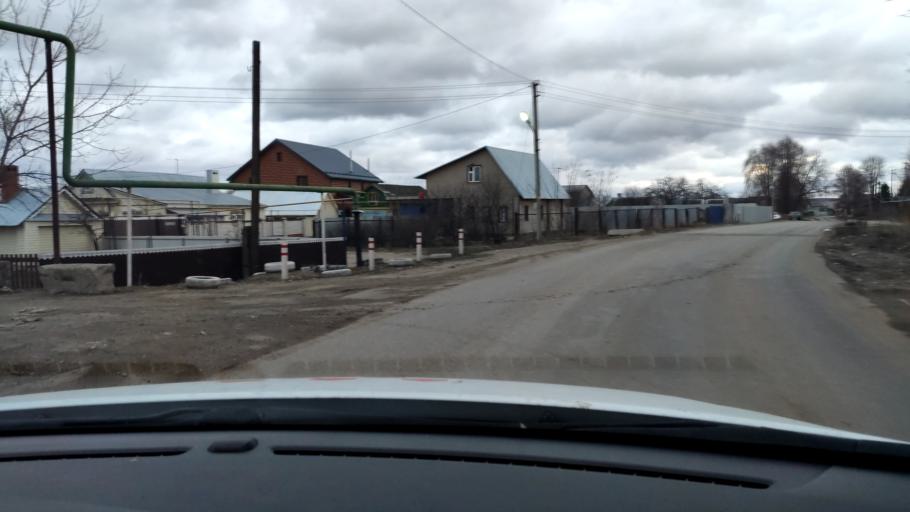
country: RU
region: Tatarstan
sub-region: Gorod Kazan'
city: Kazan
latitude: 55.7179
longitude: 49.0921
